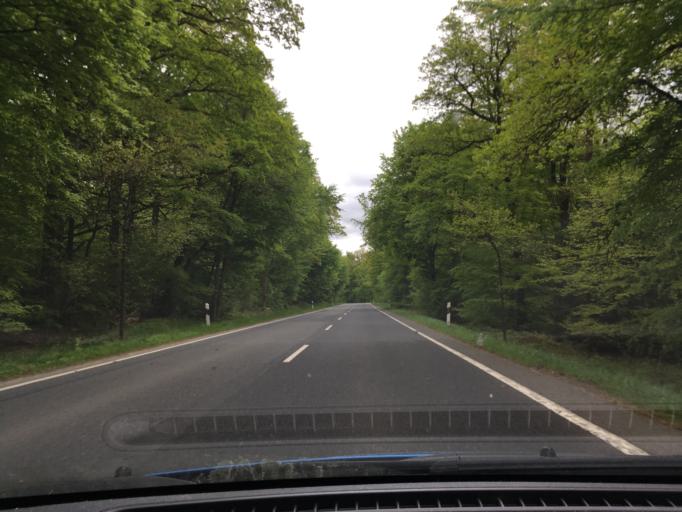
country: DE
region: Lower Saxony
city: Derental
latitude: 51.6898
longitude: 9.4912
